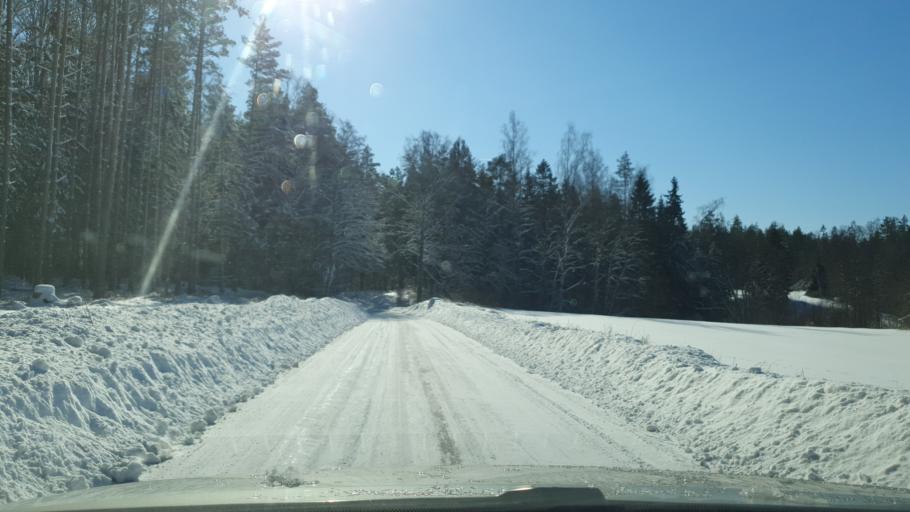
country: EE
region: Laeaene-Virumaa
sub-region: Haljala vald
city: Haljala
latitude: 59.5733
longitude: 26.1177
